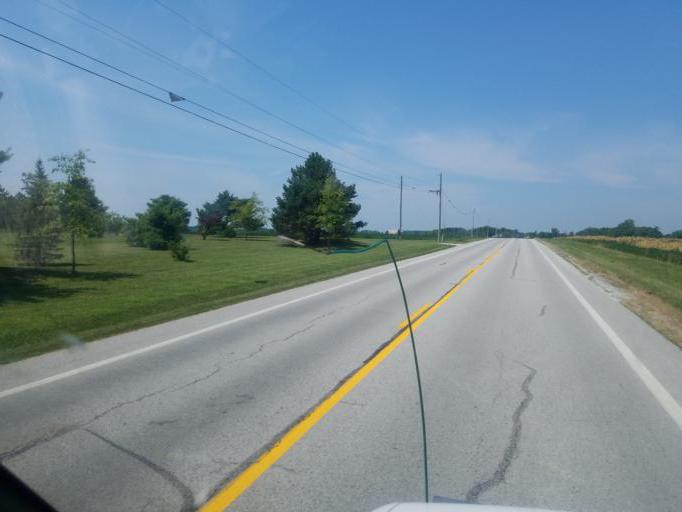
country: US
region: Ohio
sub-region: Auglaize County
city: Saint Marys
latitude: 40.4894
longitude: -84.4344
